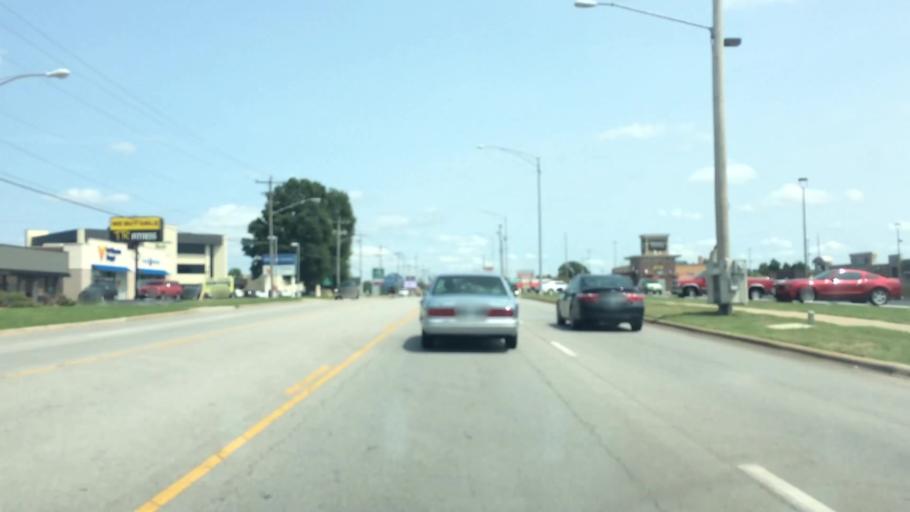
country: US
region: Missouri
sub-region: Greene County
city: Springfield
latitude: 37.1595
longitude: -93.2748
